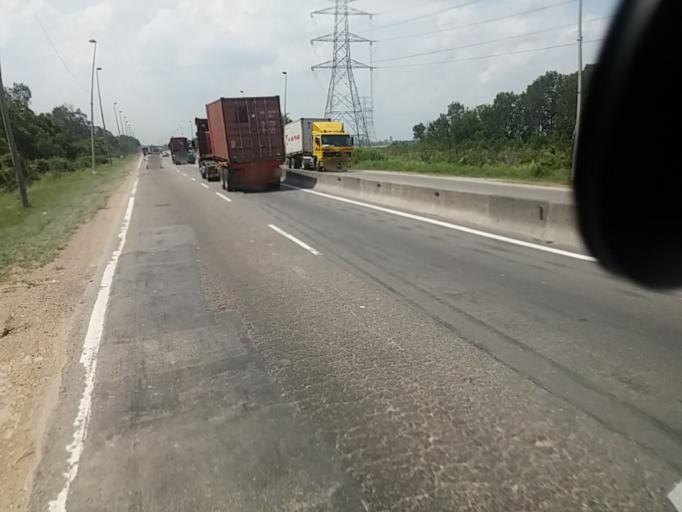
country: MY
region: Selangor
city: Klang
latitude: 2.9787
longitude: 101.3704
